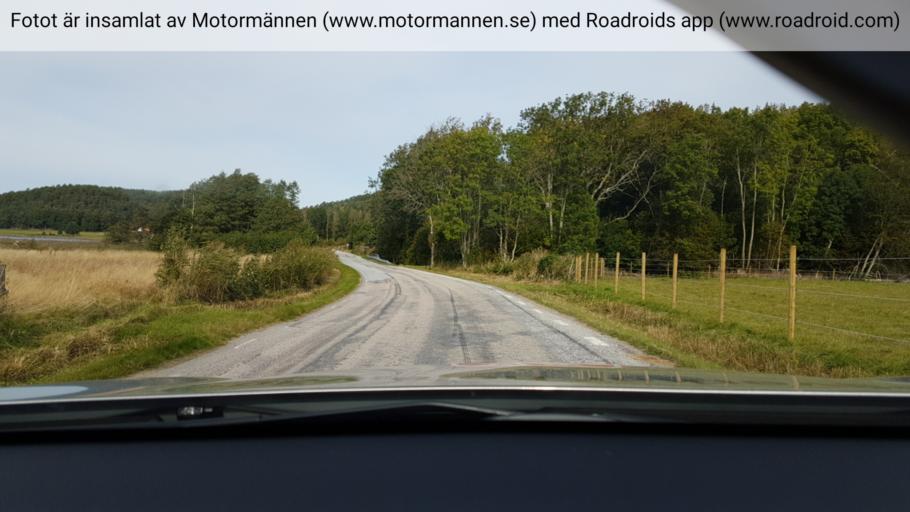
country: SE
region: Vaestra Goetaland
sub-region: Uddevalla Kommun
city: Ljungskile
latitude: 58.2538
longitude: 11.8604
